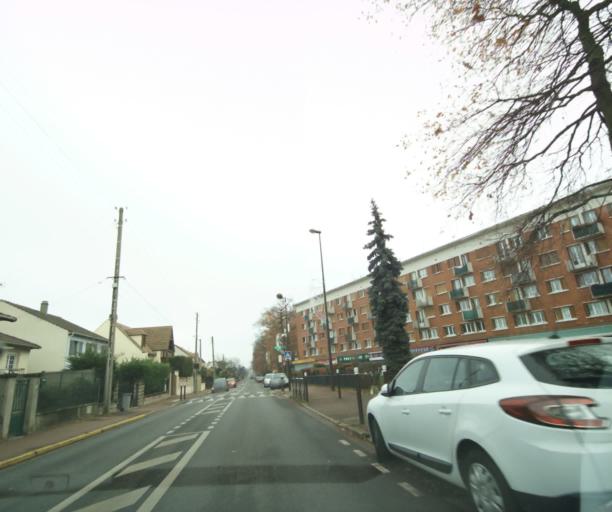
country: FR
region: Ile-de-France
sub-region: Departement de Seine-Saint-Denis
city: Livry-Gargan
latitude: 48.9212
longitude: 2.5282
